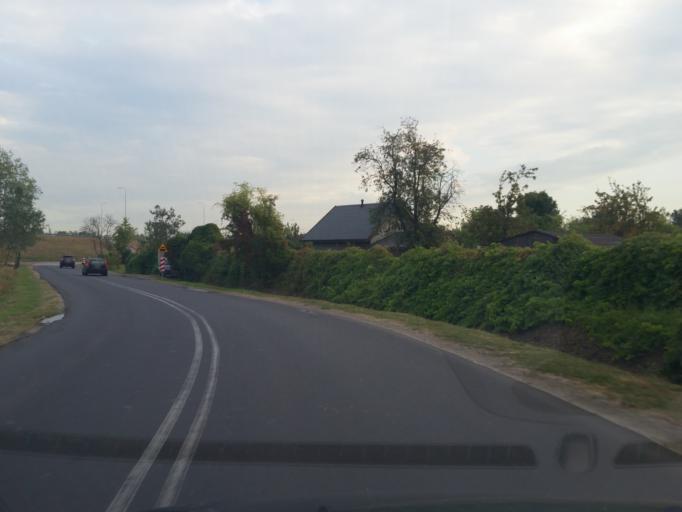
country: PL
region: Masovian Voivodeship
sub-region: Warszawa
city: Wlochy
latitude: 52.1746
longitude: 20.9840
